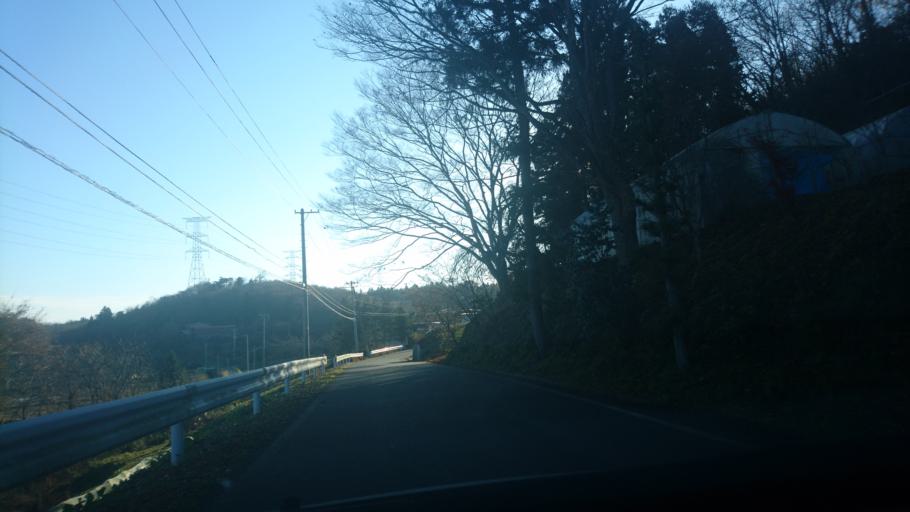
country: JP
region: Iwate
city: Ichinoseki
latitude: 38.8988
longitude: 141.2051
